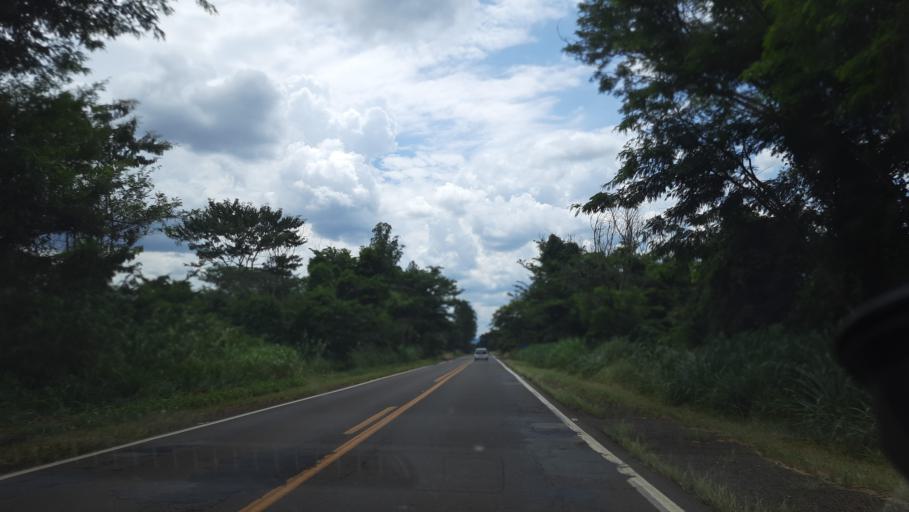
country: BR
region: Sao Paulo
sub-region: Mococa
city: Mococa
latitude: -21.4715
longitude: -47.0933
